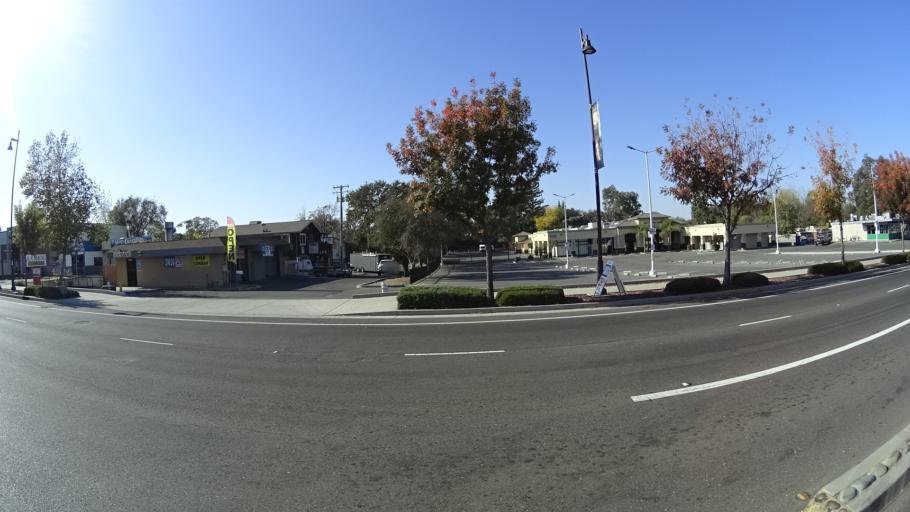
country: US
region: California
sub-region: Sacramento County
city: Citrus Heights
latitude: 38.7048
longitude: -121.2904
